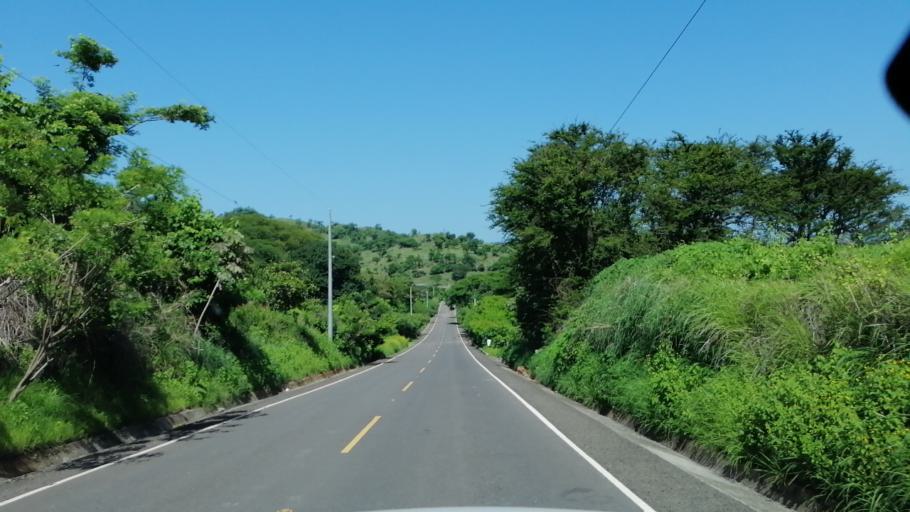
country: HN
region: Lempira
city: La Virtud
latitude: 13.9869
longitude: -88.7491
